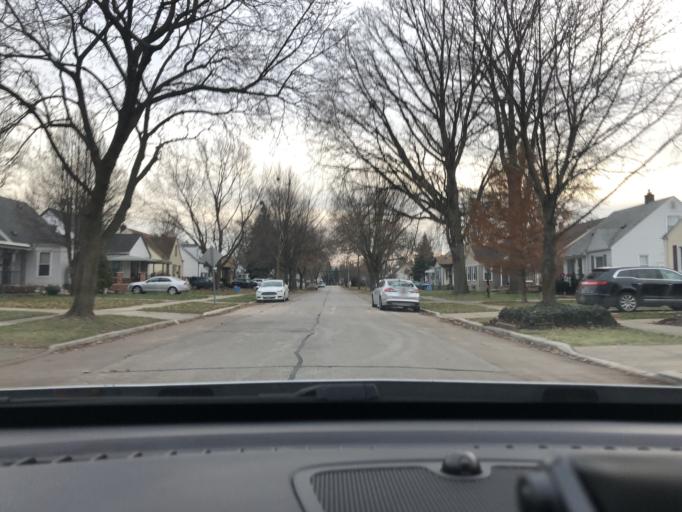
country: US
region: Michigan
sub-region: Wayne County
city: Allen Park
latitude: 42.2867
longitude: -83.2276
